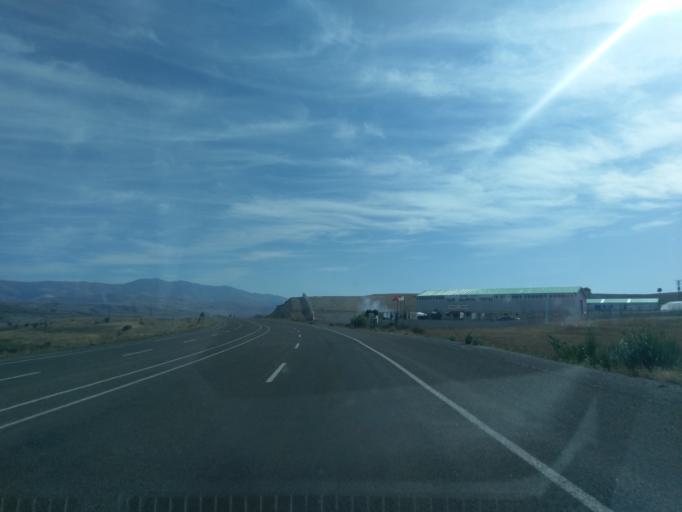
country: TR
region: Sivas
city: Imranli
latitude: 39.8704
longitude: 38.1794
